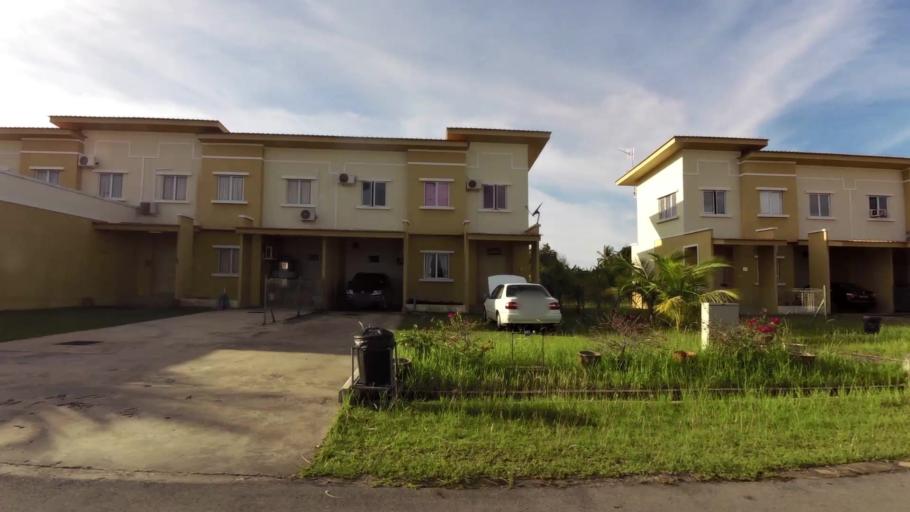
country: BN
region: Belait
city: Kuala Belait
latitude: 4.5800
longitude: 114.2232
